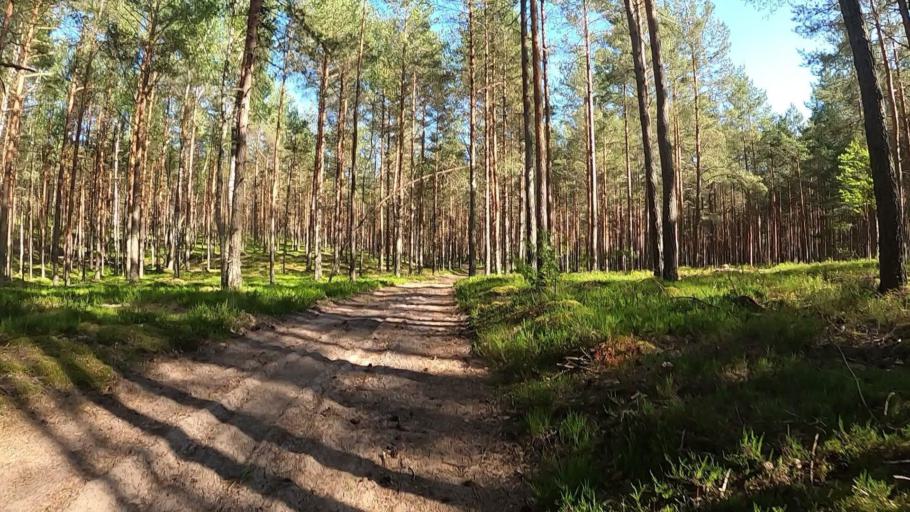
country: LV
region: Carnikava
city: Carnikava
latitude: 57.0909
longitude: 24.2553
